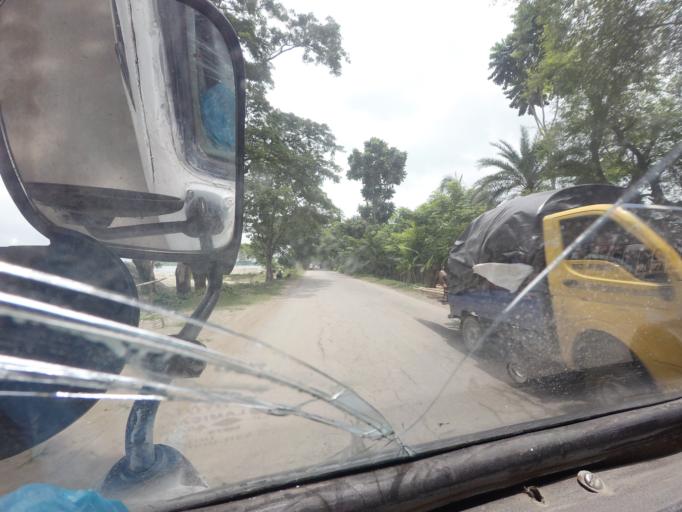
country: BD
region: Khulna
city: Kalia
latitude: 23.2000
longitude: 89.6974
